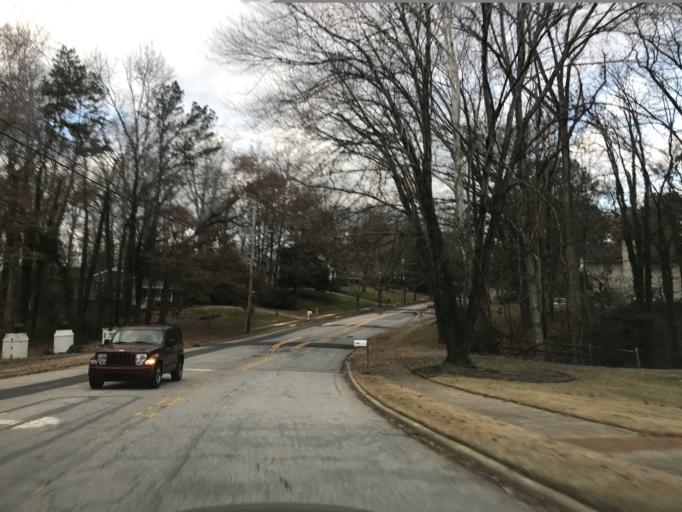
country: US
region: North Carolina
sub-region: Wake County
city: West Raleigh
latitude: 35.8442
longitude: -78.6612
